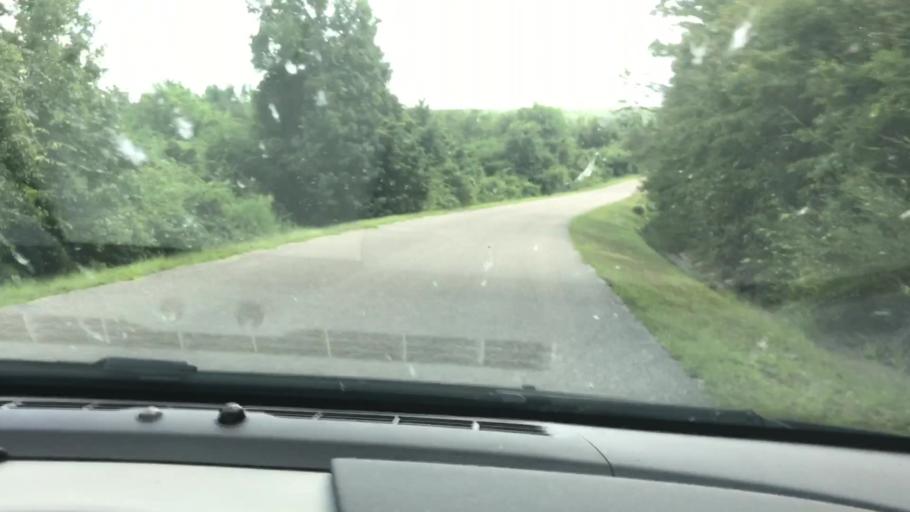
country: US
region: Georgia
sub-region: Clay County
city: Fort Gaines
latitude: 31.7403
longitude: -85.0750
